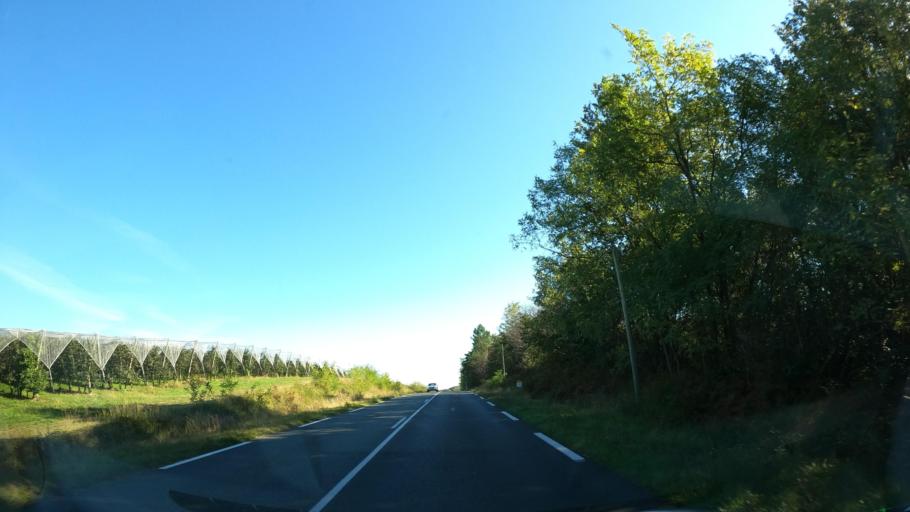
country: FR
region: Aquitaine
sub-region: Departement de la Dordogne
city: Vergt
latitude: 45.0289
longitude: 0.6252
